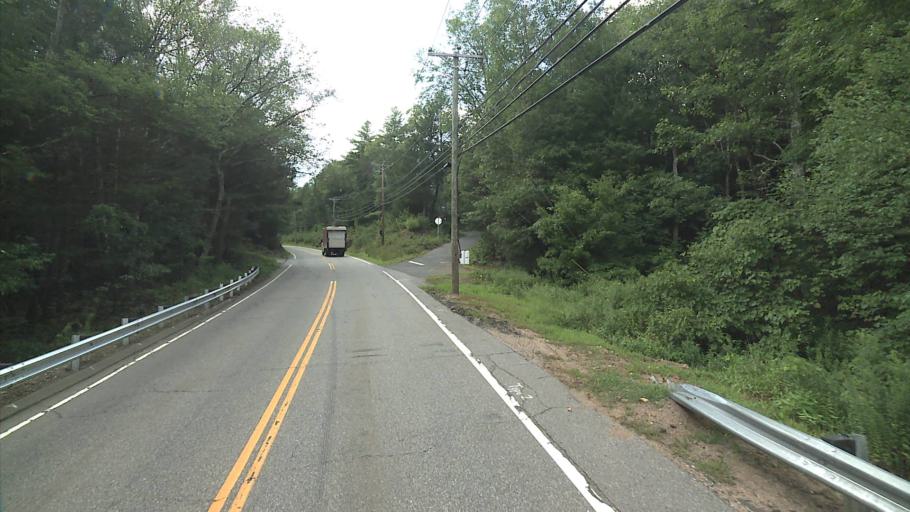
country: US
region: Connecticut
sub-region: Tolland County
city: Stafford
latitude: 41.9631
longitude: -72.2486
